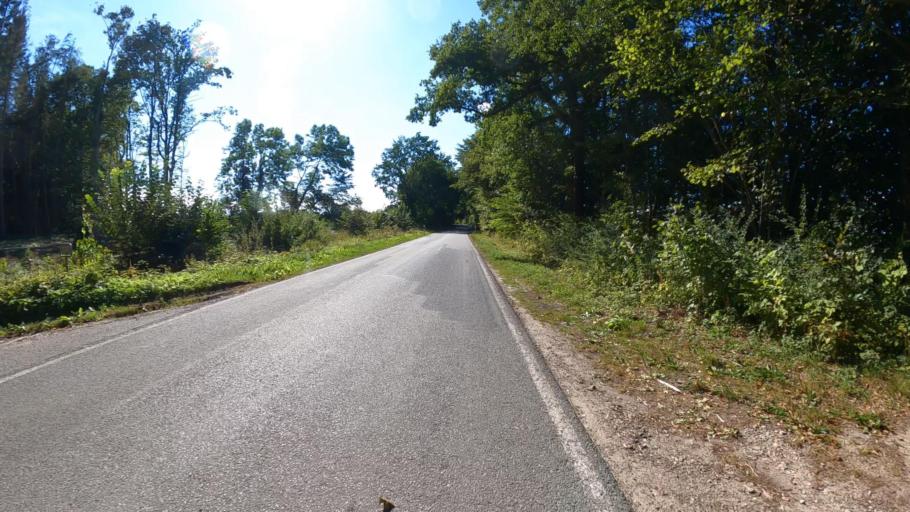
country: DE
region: Schleswig-Holstein
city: Westerau
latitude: 53.7662
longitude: 10.5065
